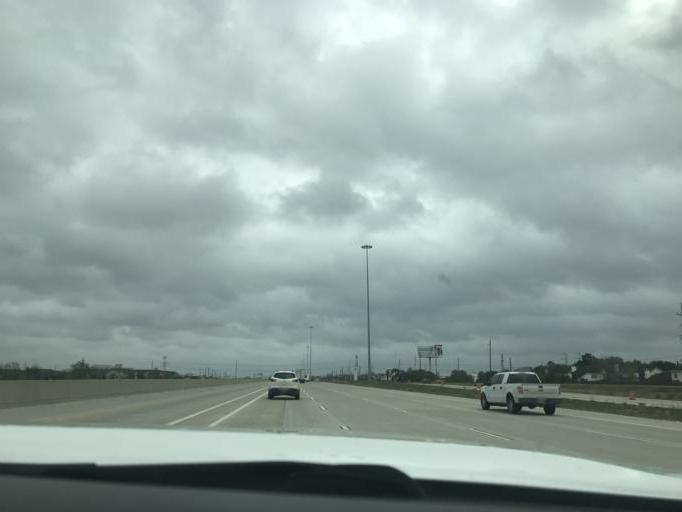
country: US
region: Texas
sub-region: Fort Bend County
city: Greatwood
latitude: 29.5590
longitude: -95.7010
